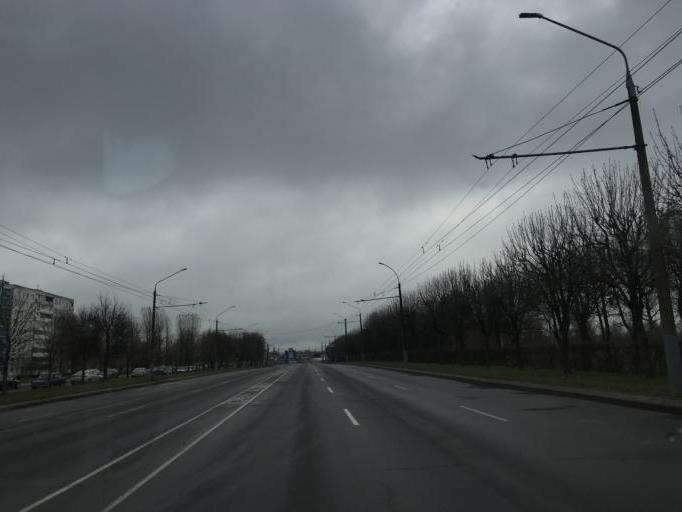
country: BY
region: Mogilev
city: Mahilyow
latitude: 53.8644
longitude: 30.3330
